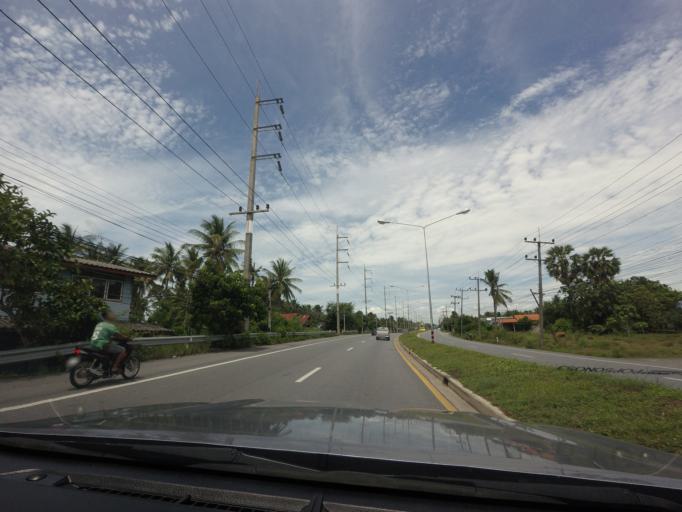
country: TH
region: Songkhla
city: Krasae Sin
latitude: 7.5964
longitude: 100.4030
